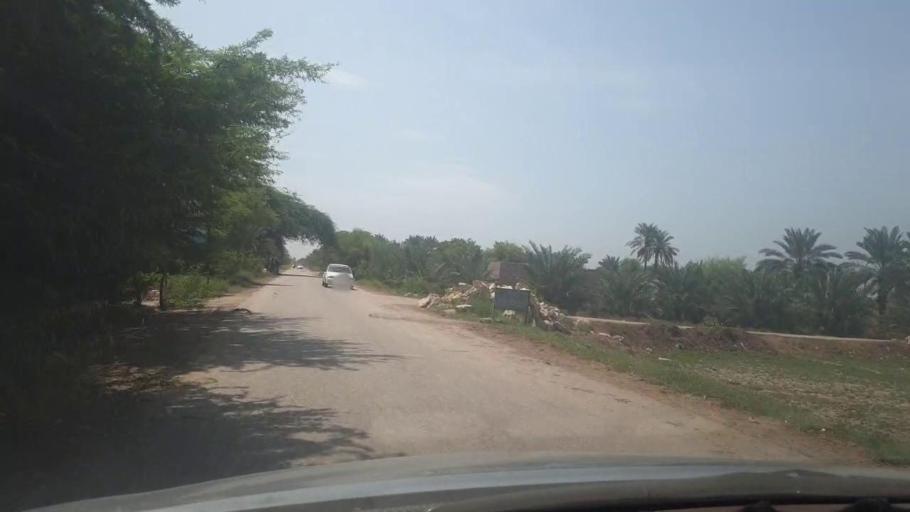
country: PK
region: Sindh
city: Bozdar
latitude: 27.2078
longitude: 68.5786
